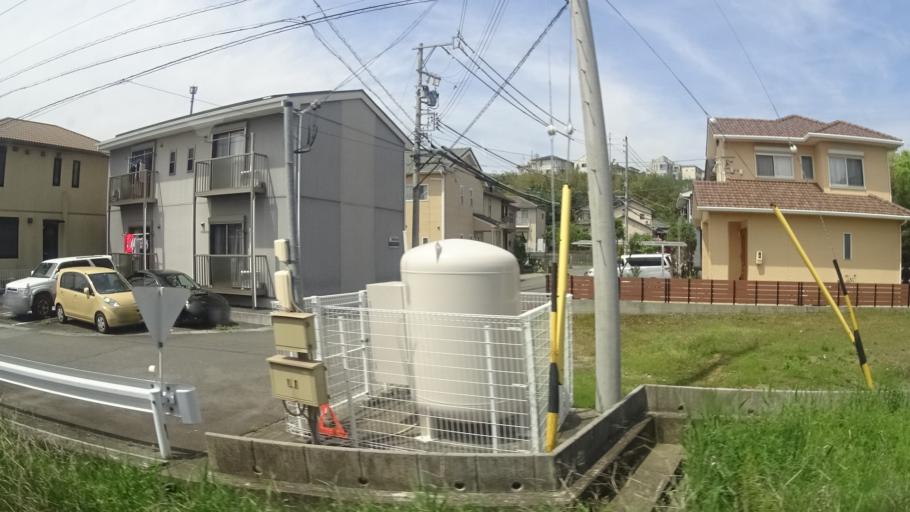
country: JP
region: Mie
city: Tsu-shi
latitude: 34.6915
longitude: 136.5089
